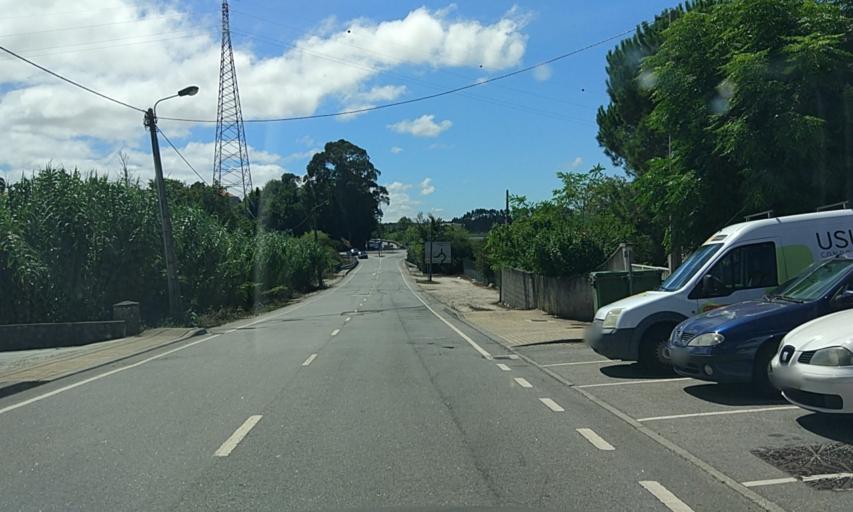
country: PT
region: Aveiro
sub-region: Ilhavo
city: Ilhavo
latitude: 40.5836
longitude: -8.6801
